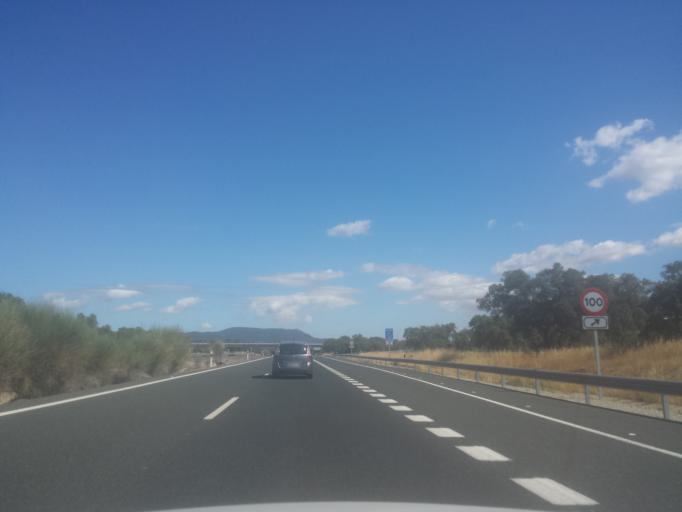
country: ES
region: Andalusia
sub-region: Provincia de Huelva
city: Santa Olalla del Cala
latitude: 37.9471
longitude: -6.2290
